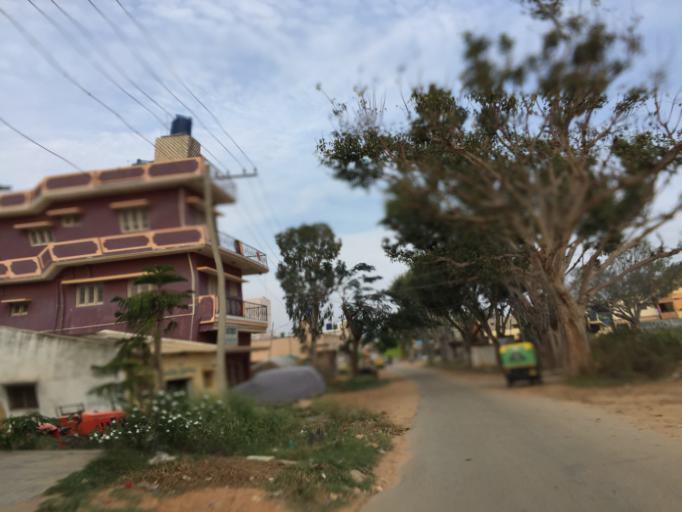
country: IN
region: Karnataka
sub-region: Kolar
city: Kolar
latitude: 13.1379
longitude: 78.1164
